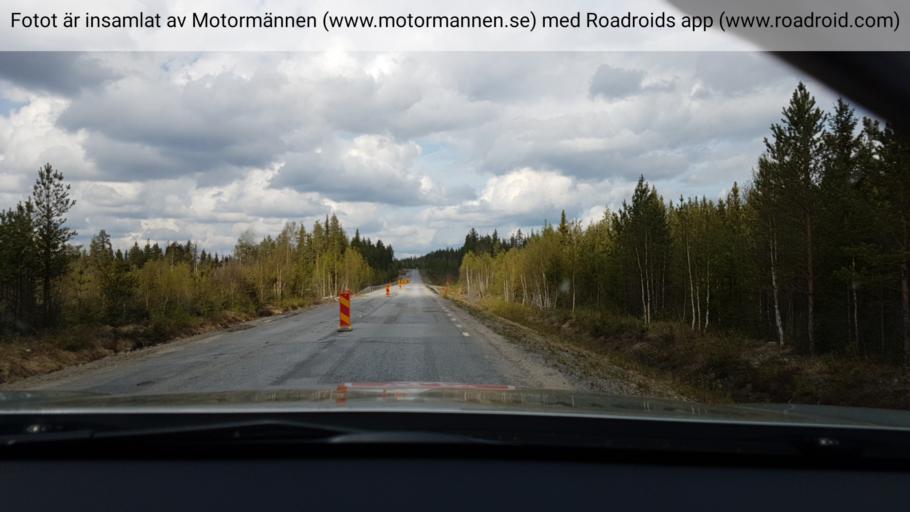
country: SE
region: Vaesternorrland
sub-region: OErnskoeldsviks Kommun
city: Bredbyn
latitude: 63.9678
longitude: 18.4987
